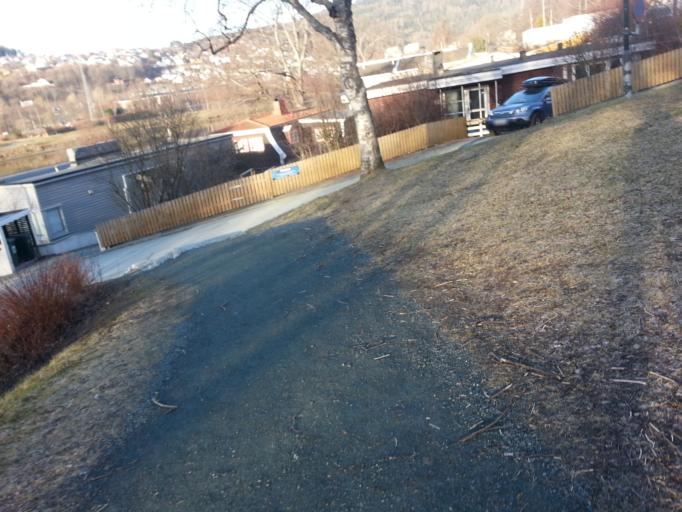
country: NO
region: Sor-Trondelag
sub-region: Trondheim
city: Trondheim
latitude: 63.4282
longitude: 10.3854
